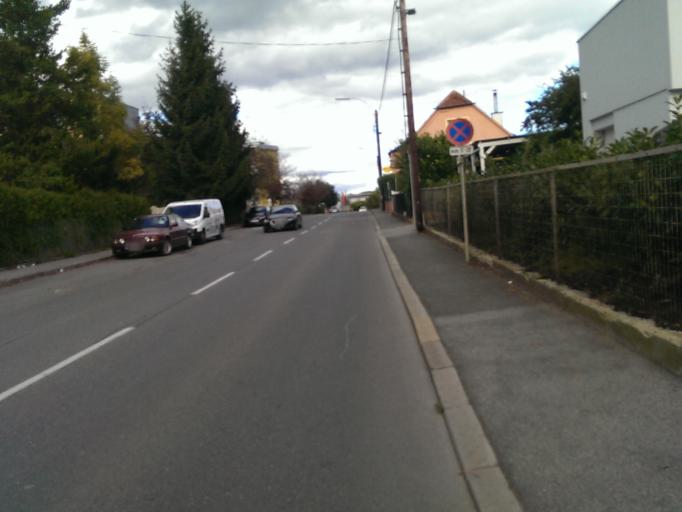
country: AT
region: Styria
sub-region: Graz Stadt
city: Graz
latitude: 47.0678
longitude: 15.4832
